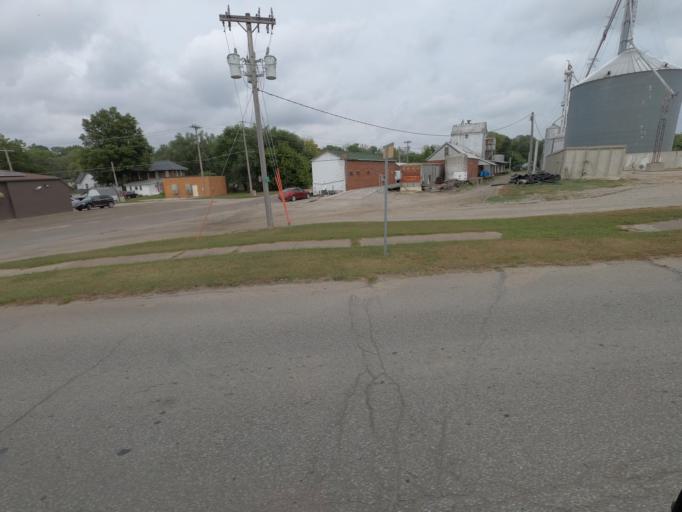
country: US
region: Iowa
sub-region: Wapello County
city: Ottumwa
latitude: 40.9179
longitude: -92.2219
